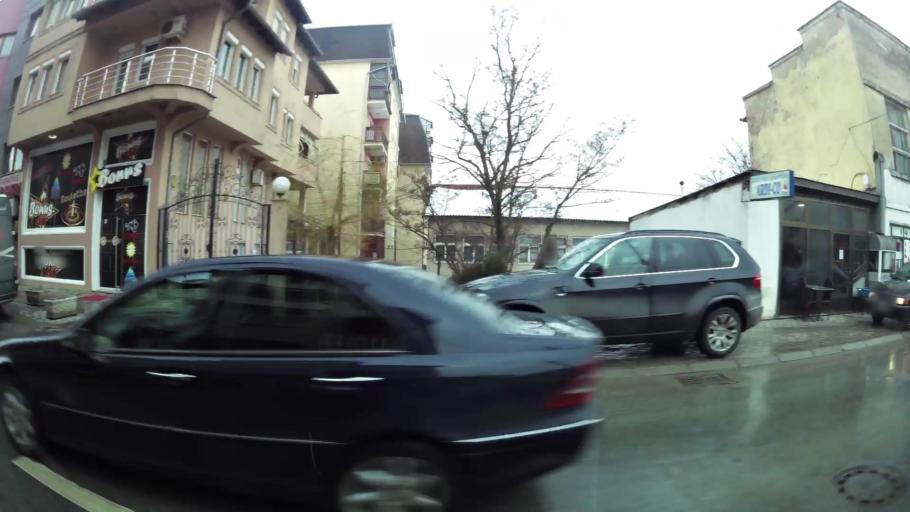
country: XK
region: Pristina
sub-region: Komuna e Prishtines
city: Pristina
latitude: 42.6670
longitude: 21.1748
